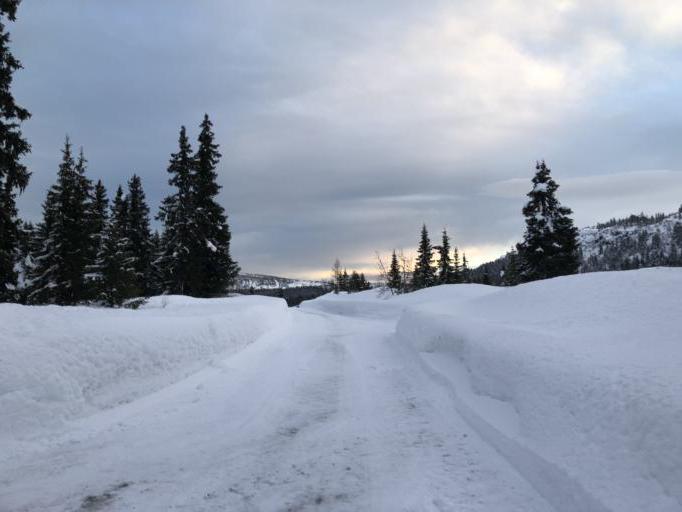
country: NO
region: Oppland
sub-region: Gausdal
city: Segalstad bru
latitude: 61.3307
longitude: 10.0521
